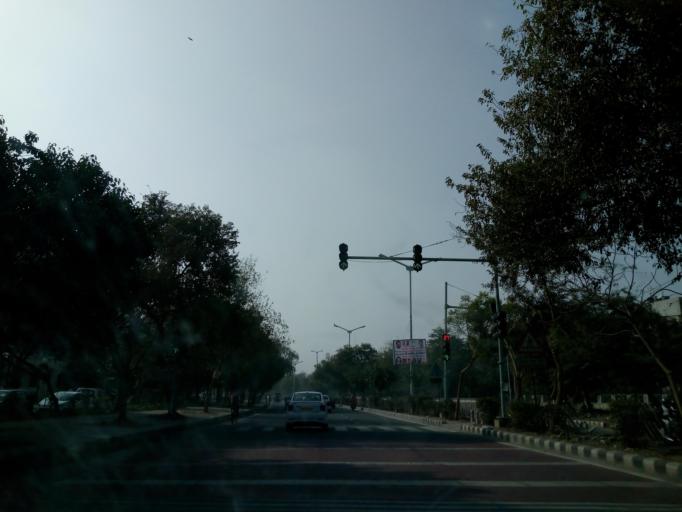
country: IN
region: NCT
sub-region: West Delhi
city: Nangloi Jat
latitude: 28.6051
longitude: 77.0508
